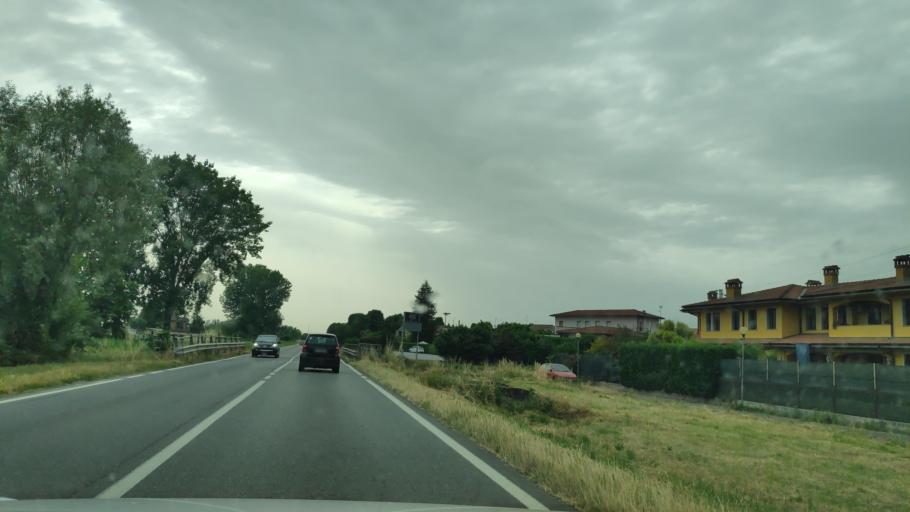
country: IT
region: Lombardy
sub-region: Provincia di Cremona
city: Romanengo
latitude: 45.3748
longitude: 9.7810
